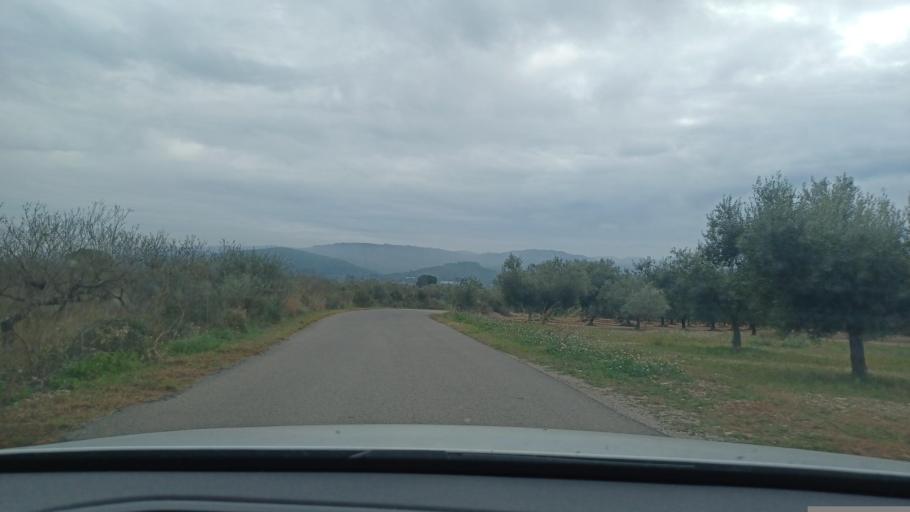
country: ES
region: Catalonia
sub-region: Provincia de Tarragona
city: Santa Barbara
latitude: 40.6675
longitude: 0.4428
